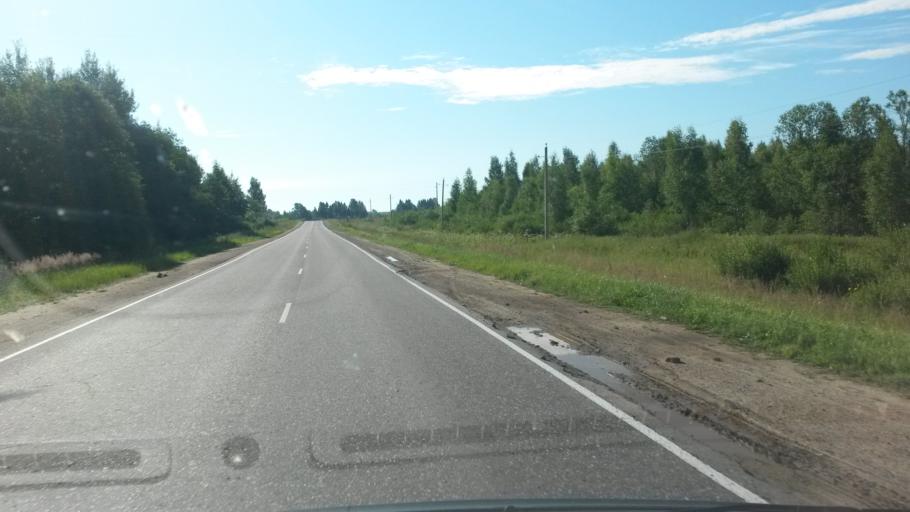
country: RU
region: Ivanovo
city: Pistsovo
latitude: 57.1605
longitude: 40.5556
